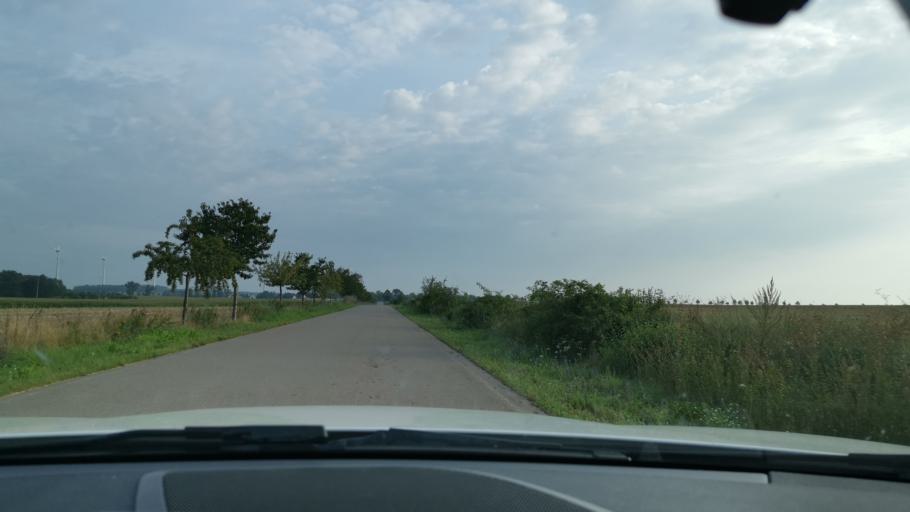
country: DE
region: Brandenburg
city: Juterbog
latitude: 51.9466
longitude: 13.1383
